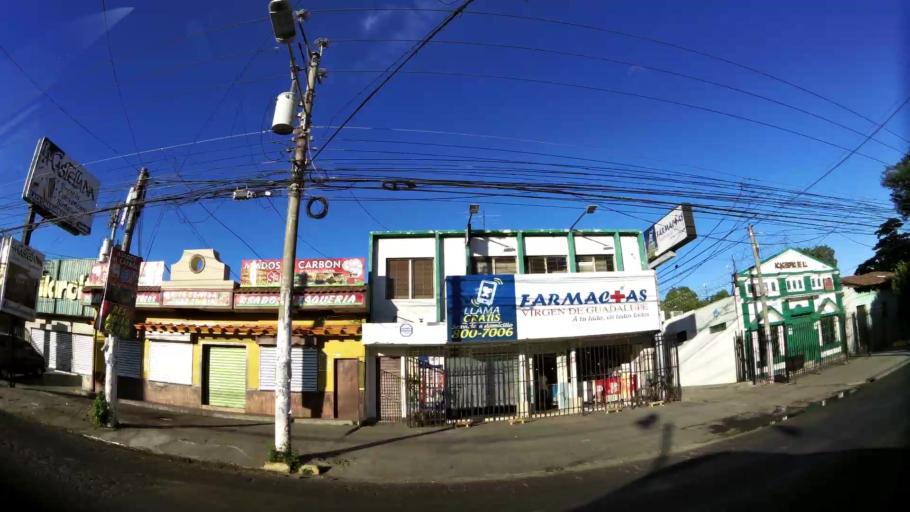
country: SV
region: San Miguel
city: San Miguel
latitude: 13.4801
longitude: -88.1848
